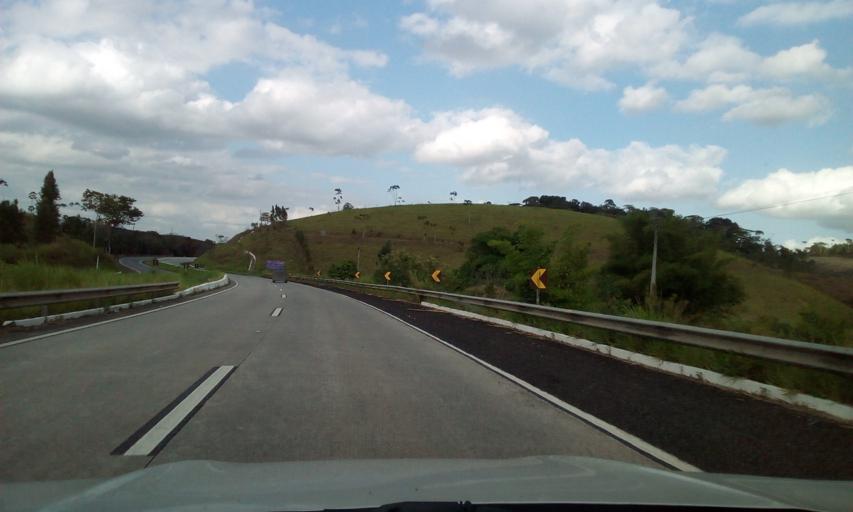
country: BR
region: Pernambuco
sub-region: Joaquim Nabuco
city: Joaquim Nabuco
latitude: -8.5702
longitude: -35.4770
